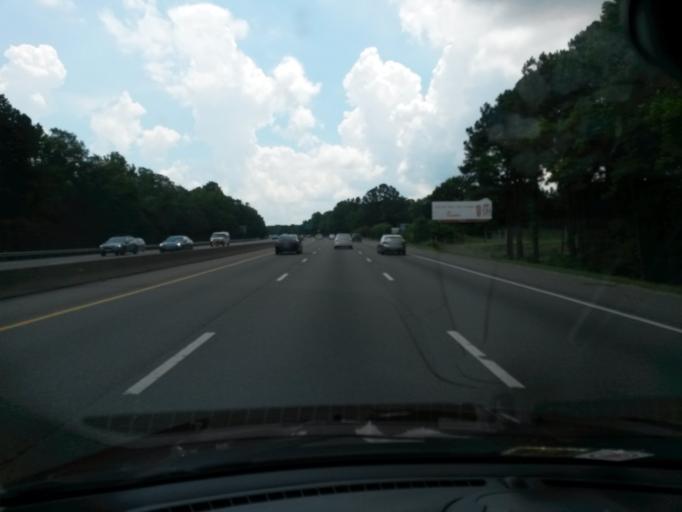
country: US
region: Virginia
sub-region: Chesterfield County
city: Bellwood
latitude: 37.3964
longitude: -77.4239
